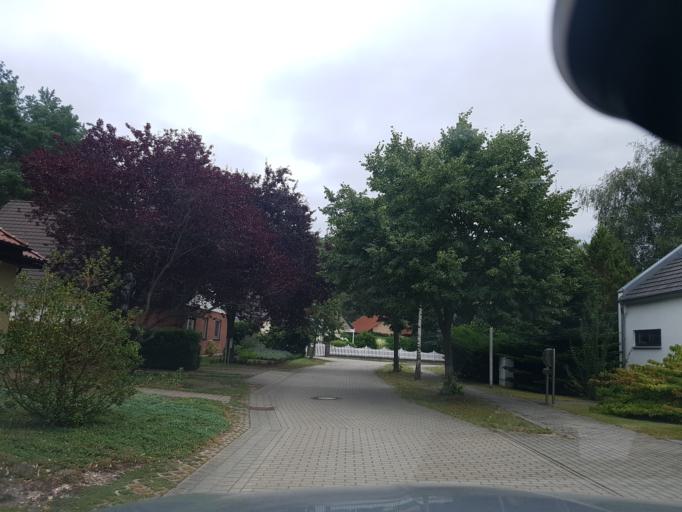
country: DE
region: Brandenburg
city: Bad Liebenwerda
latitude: 51.4981
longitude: 13.4291
